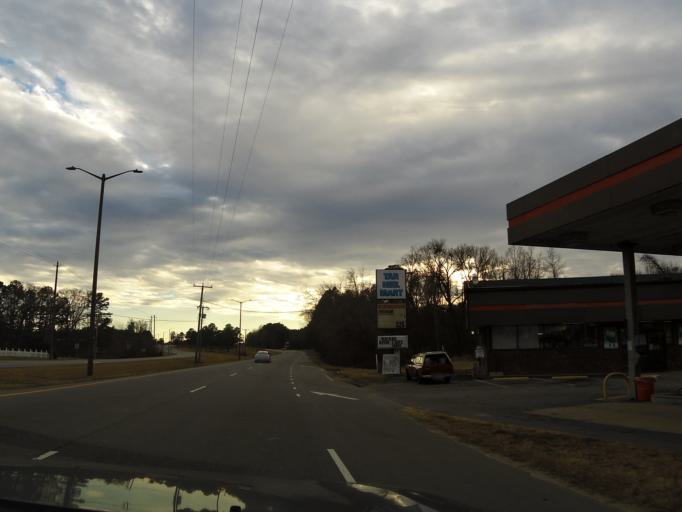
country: US
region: North Carolina
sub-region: Nash County
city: Rocky Mount
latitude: 35.9951
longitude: -77.7786
